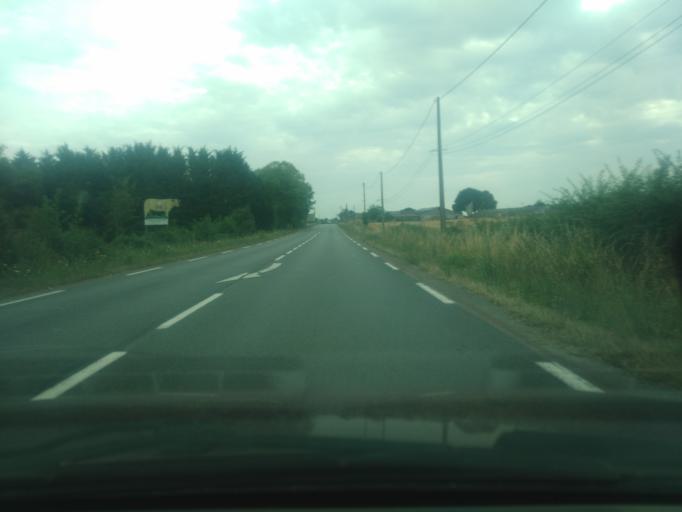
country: FR
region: Pays de la Loire
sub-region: Departement de la Vendee
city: Les Essarts
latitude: 46.7533
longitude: -1.2555
